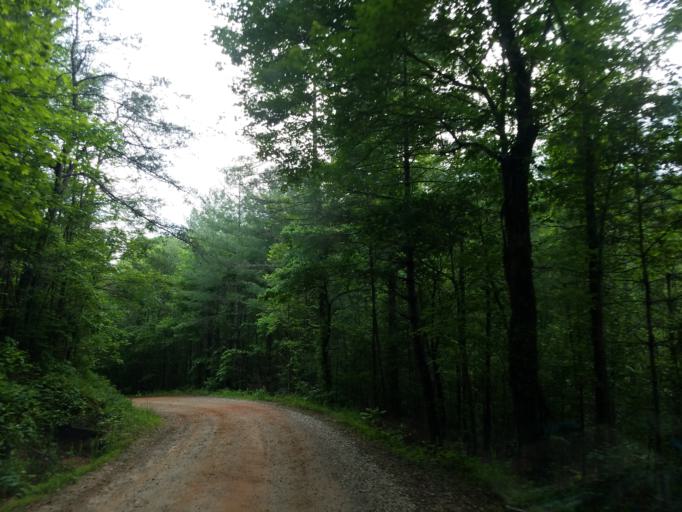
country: US
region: Georgia
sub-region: Lumpkin County
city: Dahlonega
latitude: 34.6003
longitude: -84.1100
